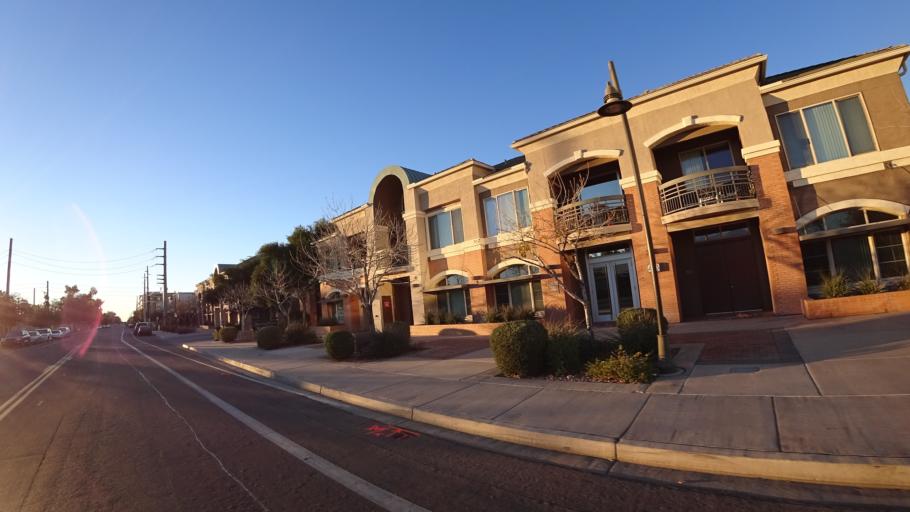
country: US
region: Arizona
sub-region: Maricopa County
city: Tempe Junction
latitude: 33.4292
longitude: -111.9447
